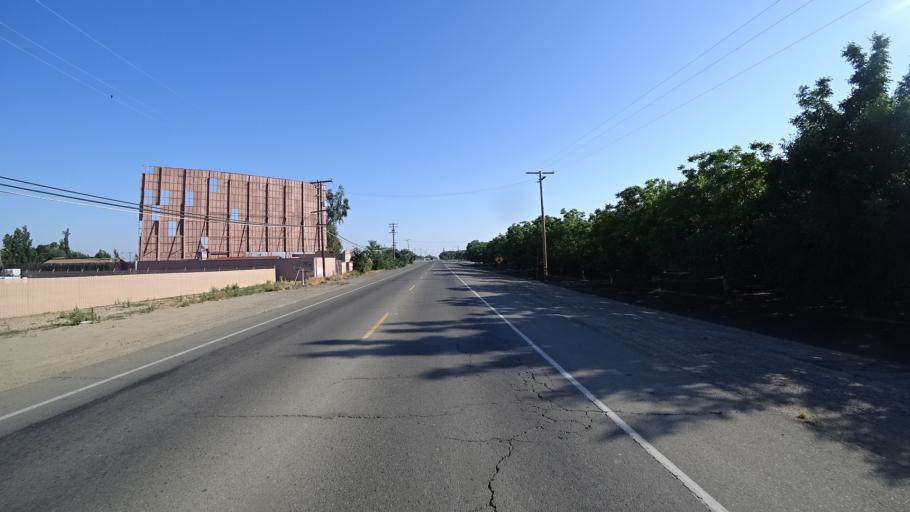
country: US
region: California
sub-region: Kings County
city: Armona
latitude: 36.3260
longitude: -119.7090
